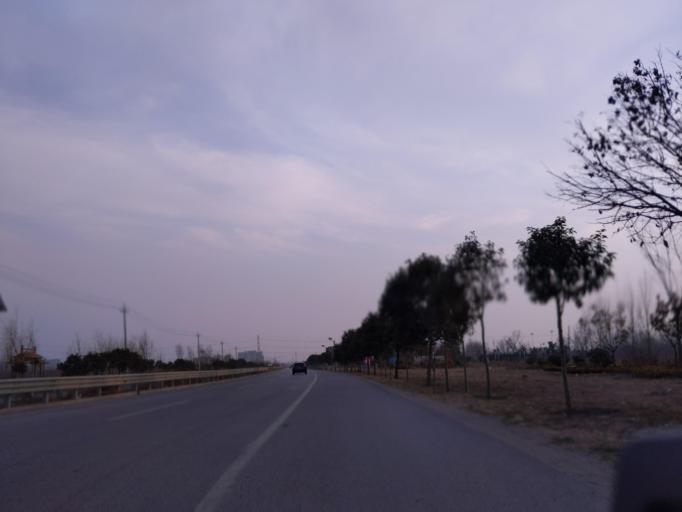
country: CN
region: Henan Sheng
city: Puyang
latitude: 35.8112
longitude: 114.9663
